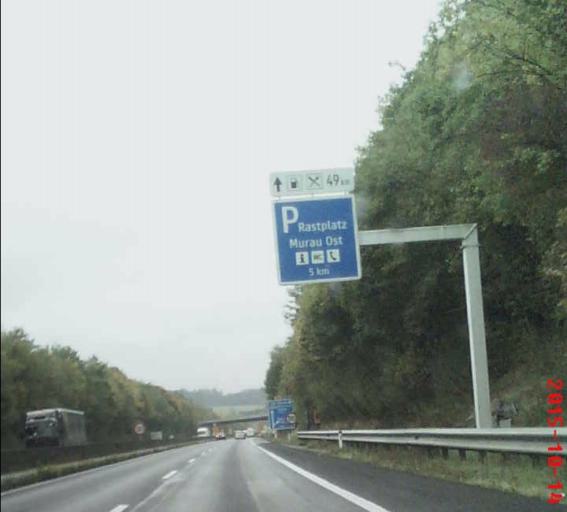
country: AT
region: Upper Austria
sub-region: Politischer Bezirk Ried im Innkreis
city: Ried im Innkreis
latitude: 48.2418
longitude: 13.5477
